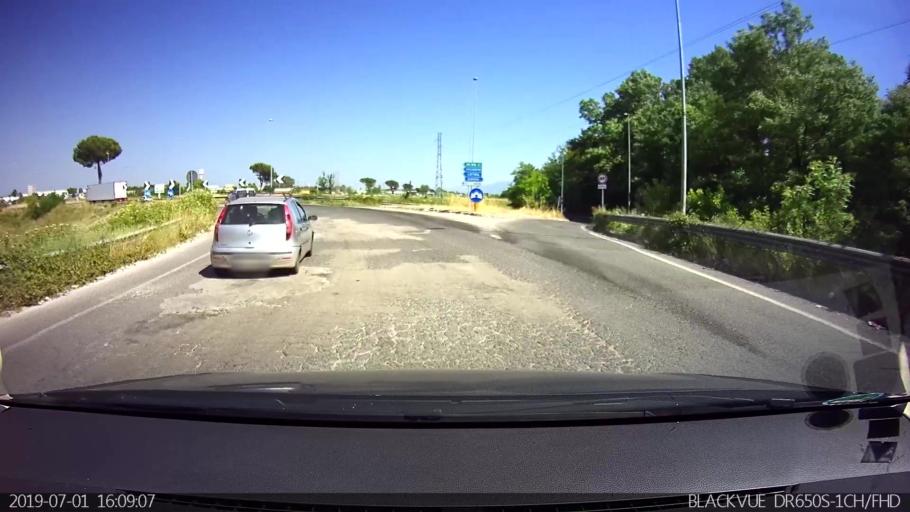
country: IT
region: Latium
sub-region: Provincia di Frosinone
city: Cartiera-Stazione
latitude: 41.6429
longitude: 13.2535
